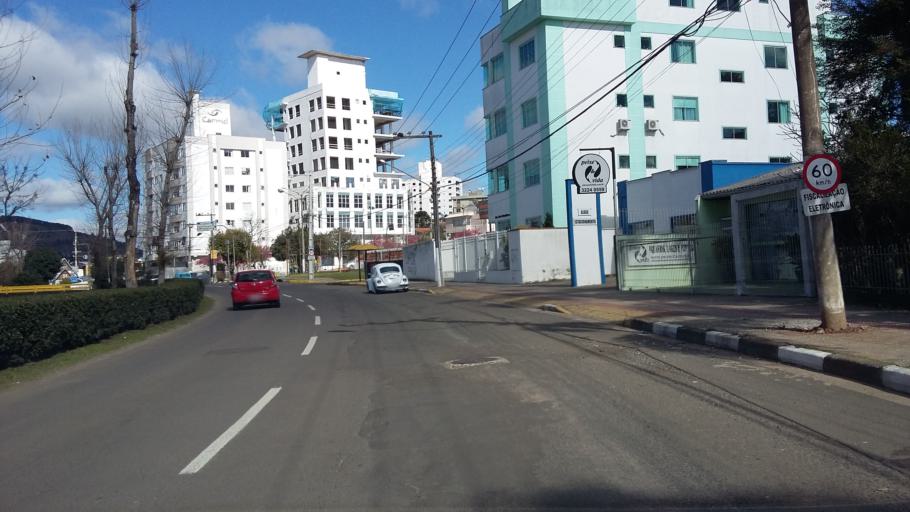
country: BR
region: Santa Catarina
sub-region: Lages
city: Lages
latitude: -27.8190
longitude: -50.3207
